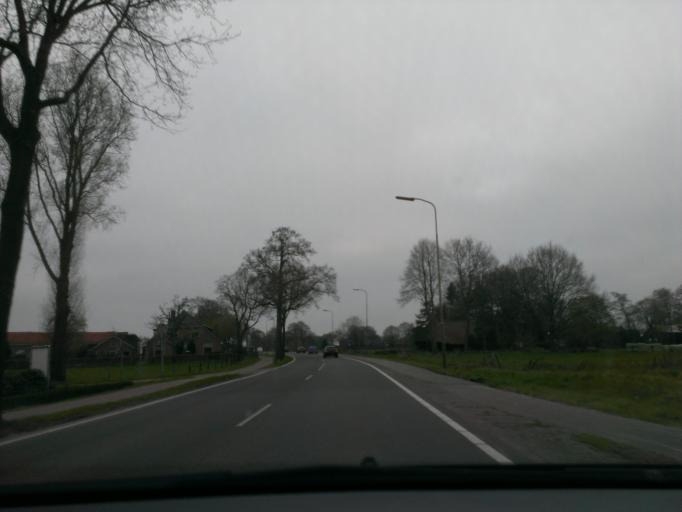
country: NL
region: Gelderland
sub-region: Gemeente Epe
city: Emst
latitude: 52.3297
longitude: 5.9815
